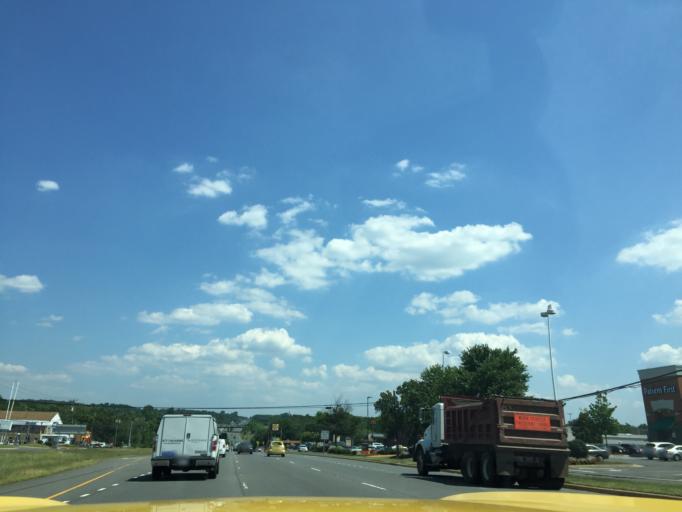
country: US
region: Virginia
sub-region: Loudoun County
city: Sugarland Run
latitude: 39.0155
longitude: -77.3736
